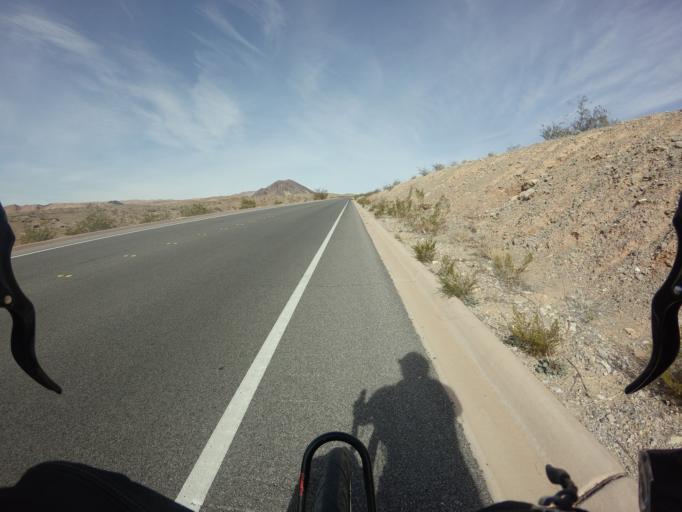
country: US
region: Nevada
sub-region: Clark County
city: Henderson
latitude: 36.1268
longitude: -114.9048
